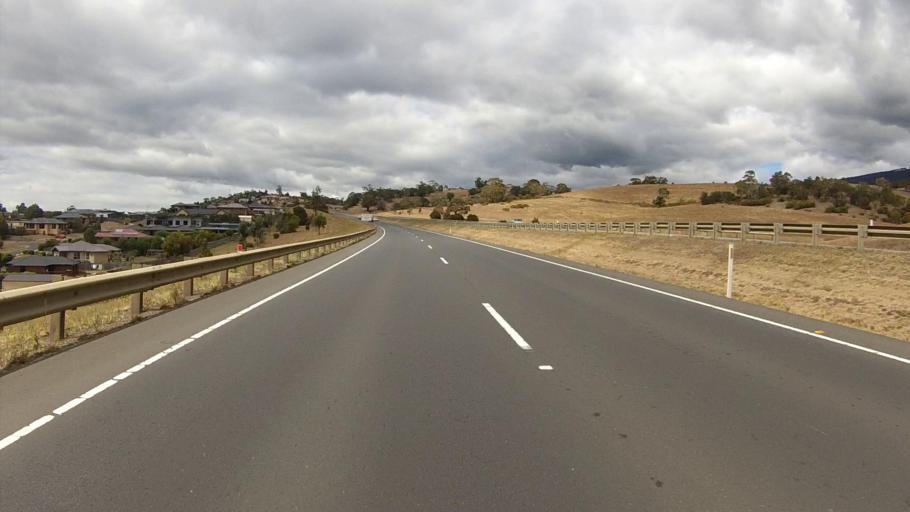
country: AU
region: Tasmania
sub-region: Glenorchy
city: Austins Ferry
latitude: -42.7659
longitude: 147.2356
